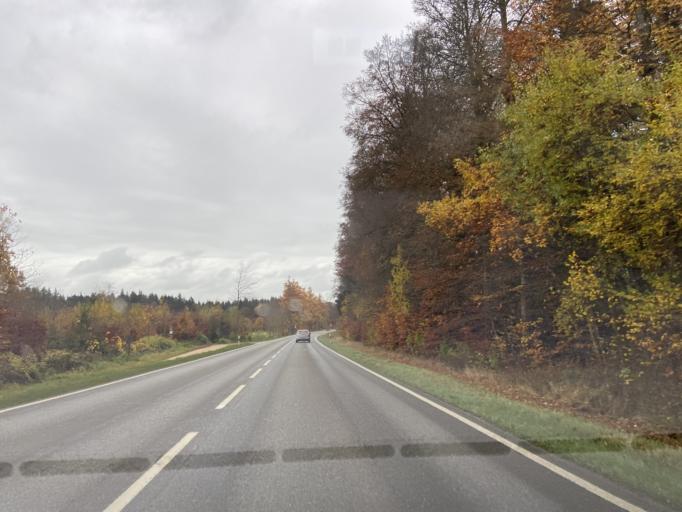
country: DE
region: Baden-Wuerttemberg
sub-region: Tuebingen Region
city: Sigmaringen
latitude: 48.0589
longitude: 9.2299
